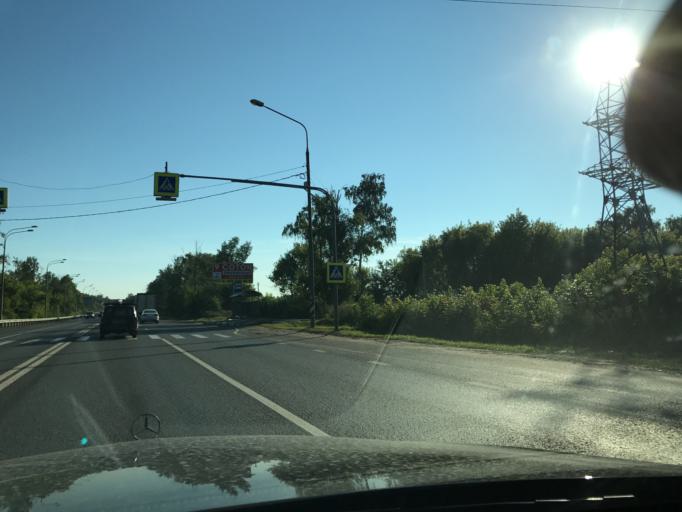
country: RU
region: Moskovskaya
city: Medvezh'i Ozera
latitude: 55.8464
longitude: 37.9601
